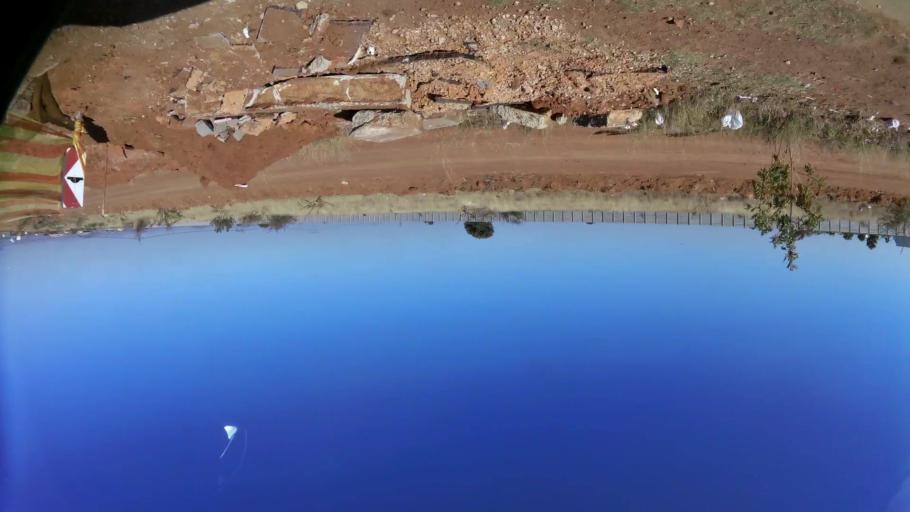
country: ZA
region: Gauteng
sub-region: City of Tshwane Metropolitan Municipality
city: Mabopane
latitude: -25.5550
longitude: 28.0953
